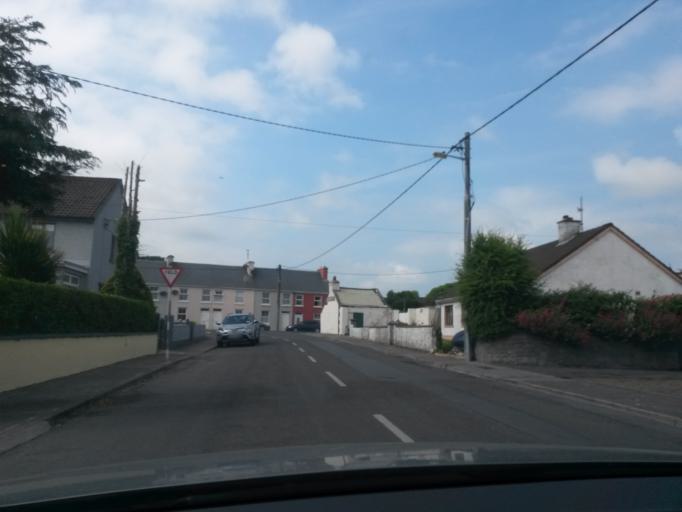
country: IE
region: Munster
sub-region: An Clar
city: Kilrush
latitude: 52.6377
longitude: -9.4894
